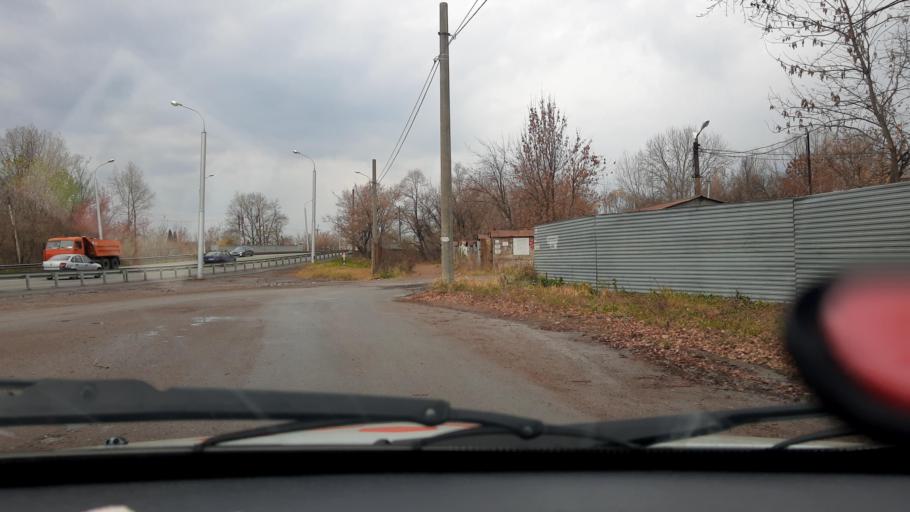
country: RU
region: Bashkortostan
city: Ufa
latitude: 54.8063
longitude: 56.1512
